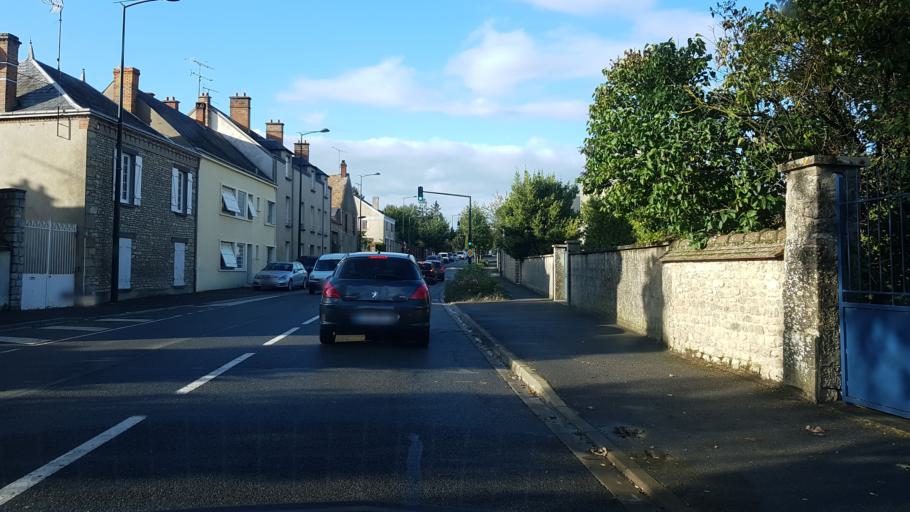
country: FR
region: Centre
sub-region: Departement du Loiret
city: Sermaises
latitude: 48.2977
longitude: 2.2005
